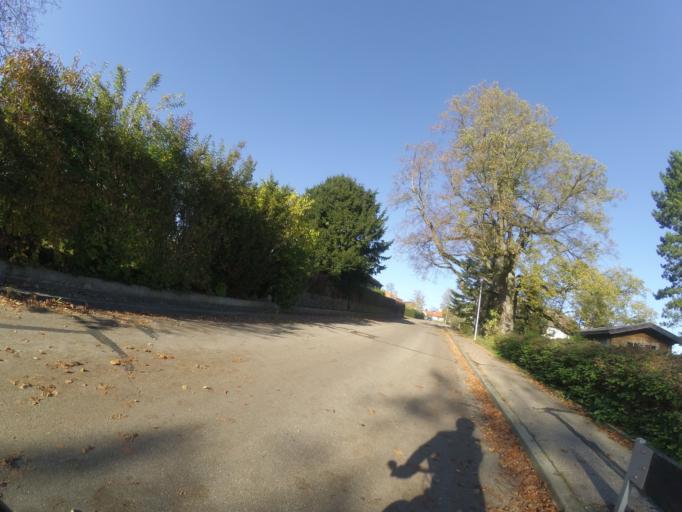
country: DE
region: Baden-Wuerttemberg
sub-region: Tuebingen Region
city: Blaubeuren
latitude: 48.4135
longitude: 9.8088
